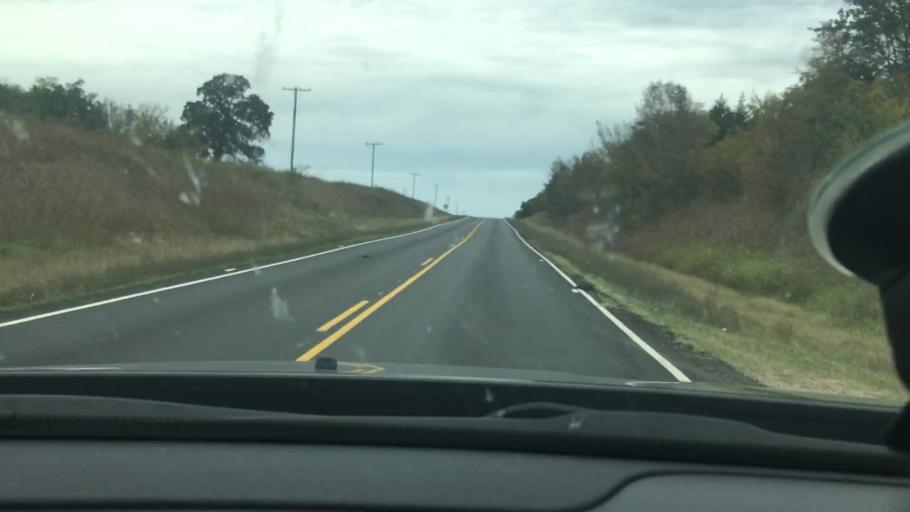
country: US
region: Oklahoma
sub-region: Coal County
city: Coalgate
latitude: 34.4075
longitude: -96.4243
